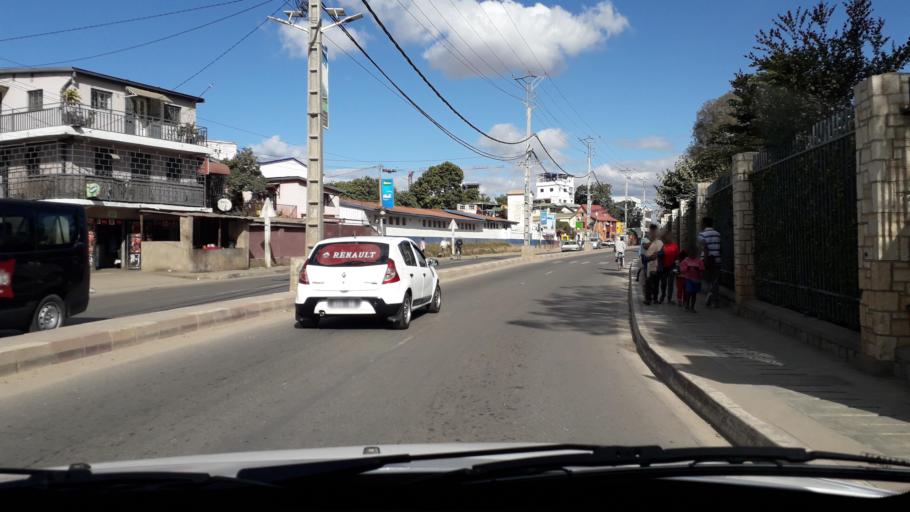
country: MG
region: Analamanga
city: Antananarivo
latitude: -18.8692
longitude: 47.5177
